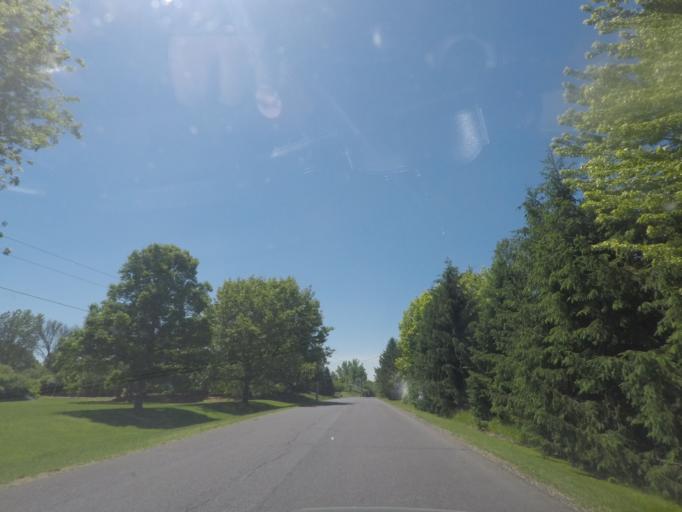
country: US
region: New York
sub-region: Saratoga County
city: Country Knolls
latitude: 42.9434
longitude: -73.7648
